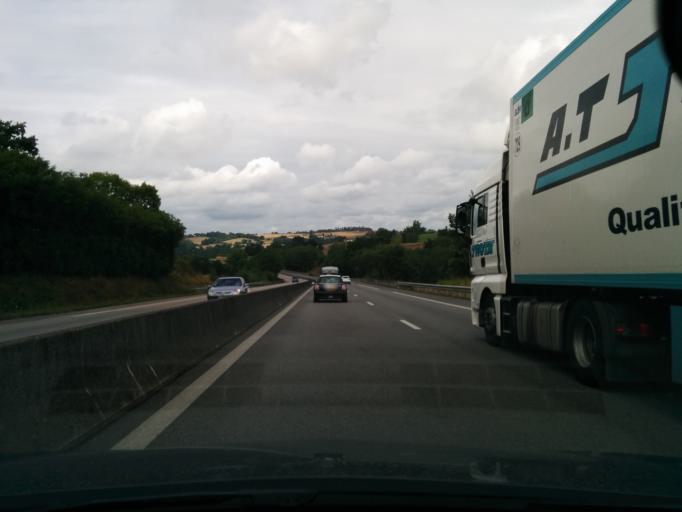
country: FR
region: Limousin
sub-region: Departement de la Haute-Vienne
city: Pierre-Buffiere
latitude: 45.7207
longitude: 1.3510
